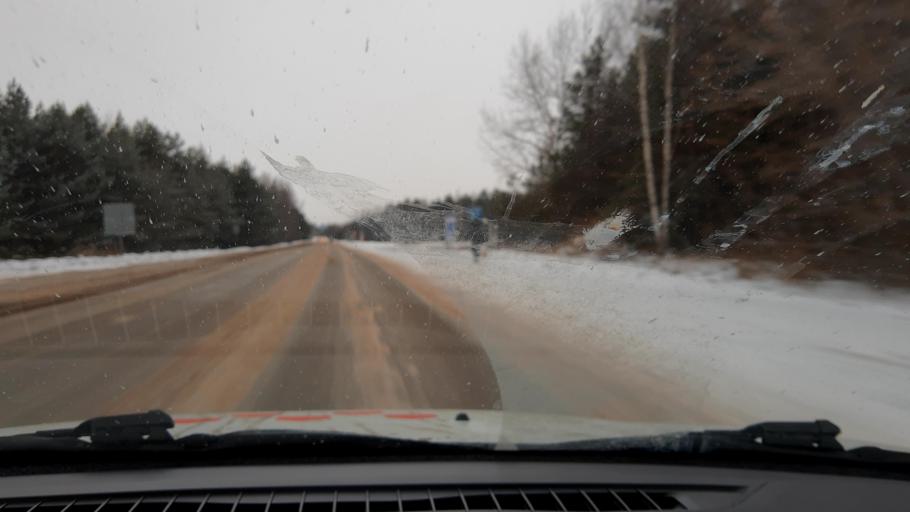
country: RU
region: Nizjnij Novgorod
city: Bor
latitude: 56.3244
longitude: 44.1431
